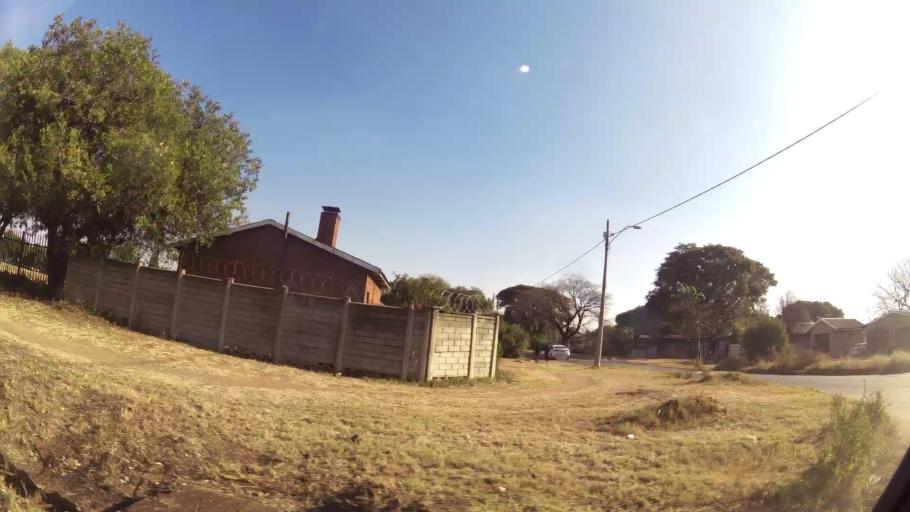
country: ZA
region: North-West
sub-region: Bojanala Platinum District Municipality
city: Rustenburg
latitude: -25.6566
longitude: 27.2572
